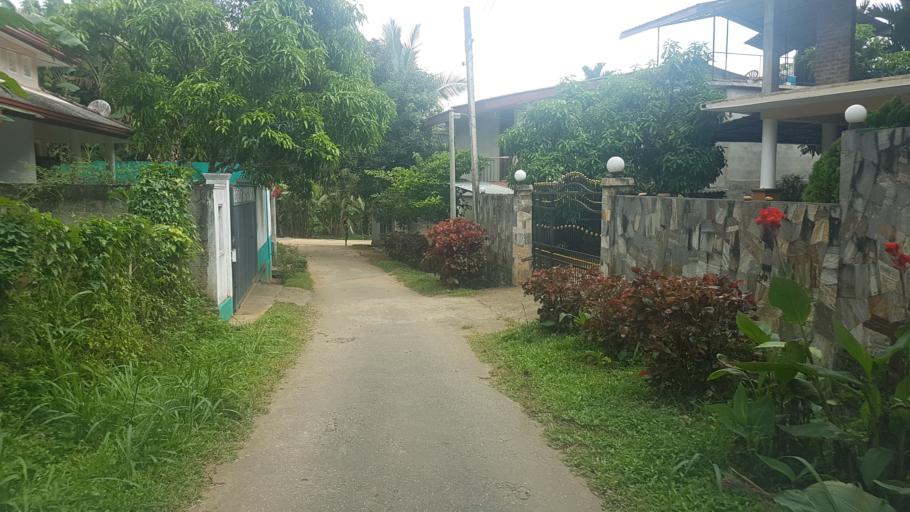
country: LK
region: Central
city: Gampola
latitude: 7.2226
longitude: 80.5848
